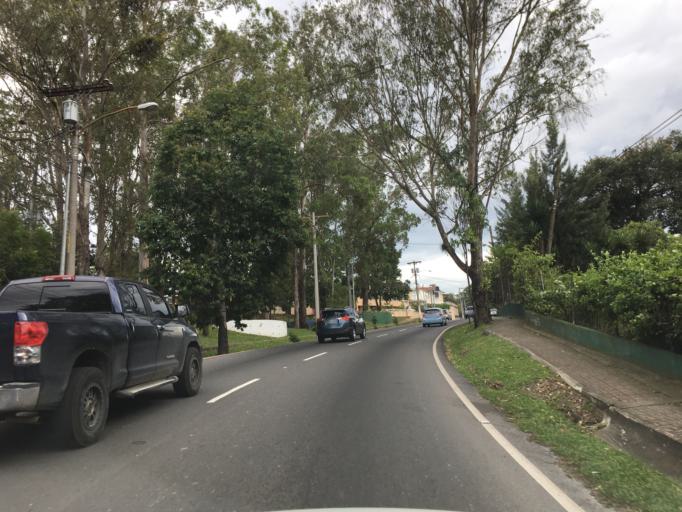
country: GT
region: Guatemala
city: Mixco
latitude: 14.5950
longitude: -90.5673
